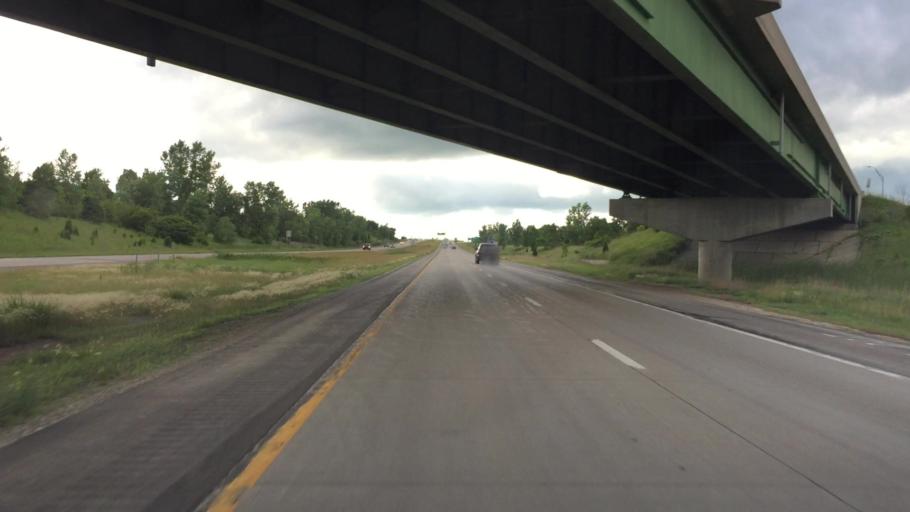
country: US
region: Iowa
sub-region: Polk County
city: Altoona
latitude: 41.6333
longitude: -93.5032
